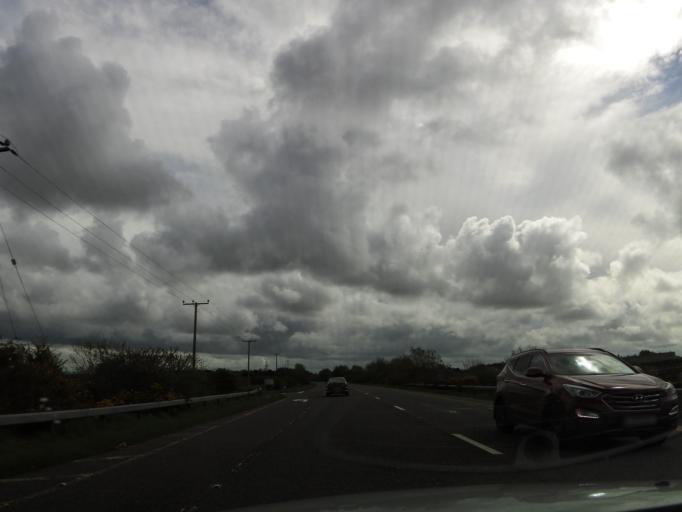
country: IE
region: Connaught
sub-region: Maigh Eo
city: Claremorris
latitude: 53.7142
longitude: -8.9858
